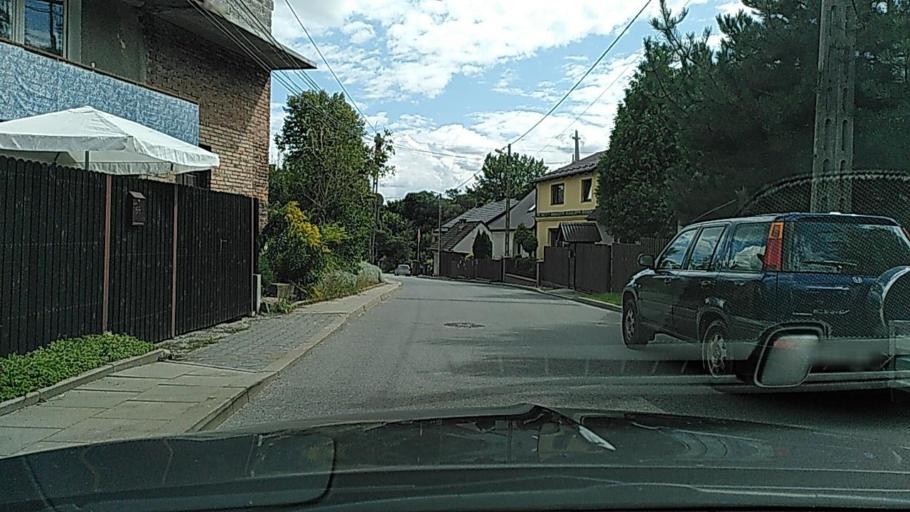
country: PL
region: Lesser Poland Voivodeship
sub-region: Powiat krakowski
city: Rzaska
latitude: 50.0890
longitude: 19.8729
